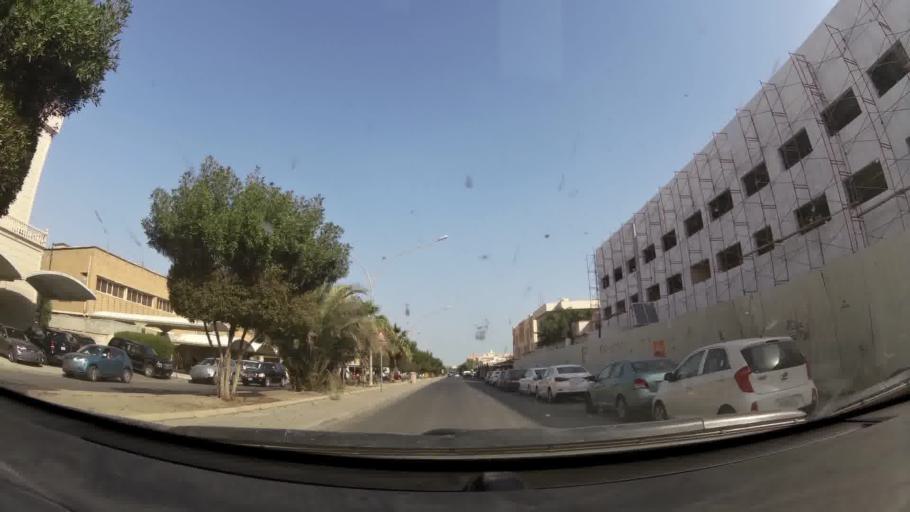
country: KW
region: Muhafazat Hawalli
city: Salwa
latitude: 29.2841
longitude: 48.0796
